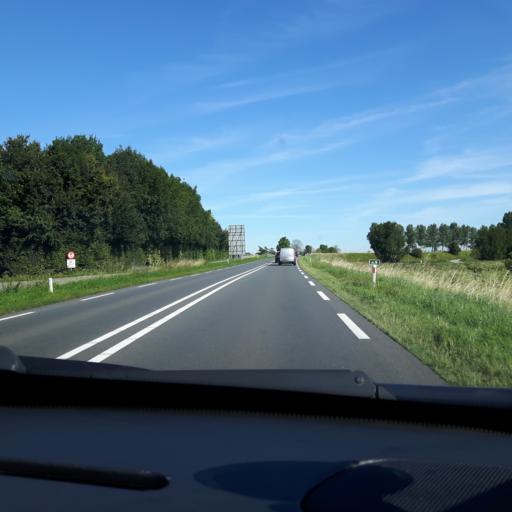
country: NL
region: Zeeland
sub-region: Gemeente Goes
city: Goes
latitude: 51.5140
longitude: 3.8686
